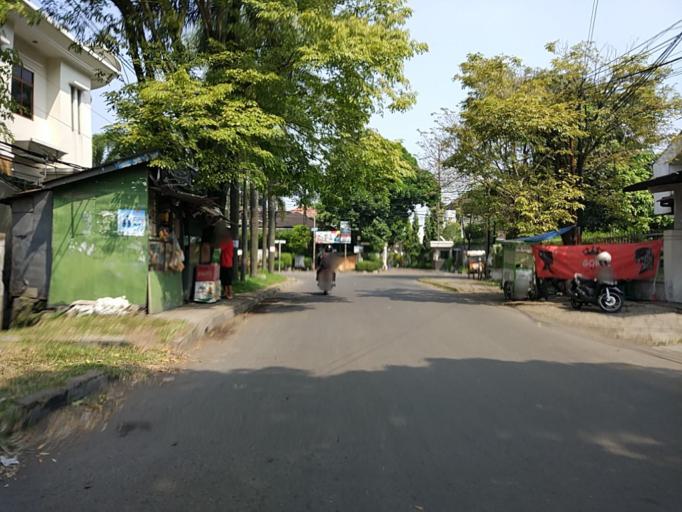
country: ID
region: West Java
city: Margahayukencana
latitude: -6.9379
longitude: 107.5733
